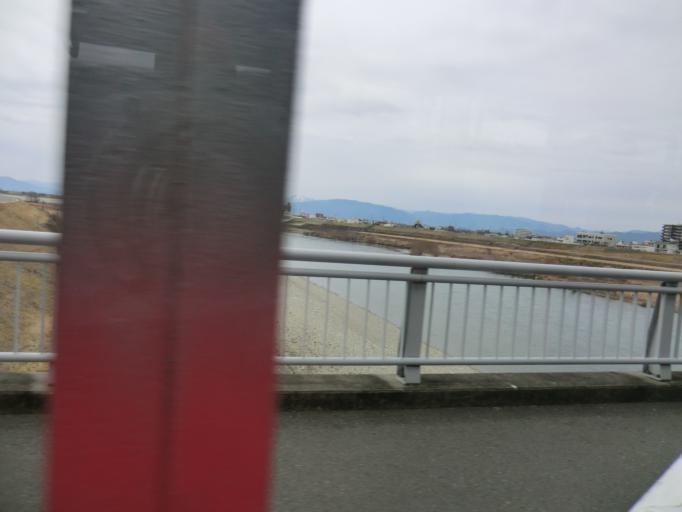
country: JP
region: Gifu
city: Gifu-shi
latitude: 35.4292
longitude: 136.7504
